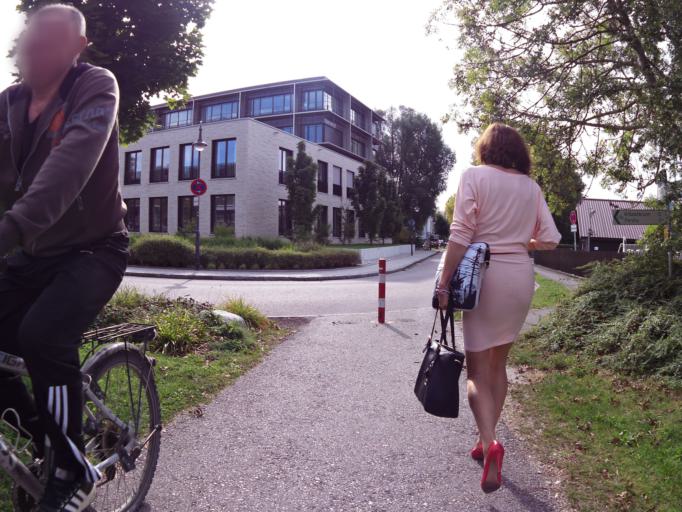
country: DE
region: Bavaria
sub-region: Upper Bavaria
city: Starnberg
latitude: 48.0004
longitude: 11.3576
